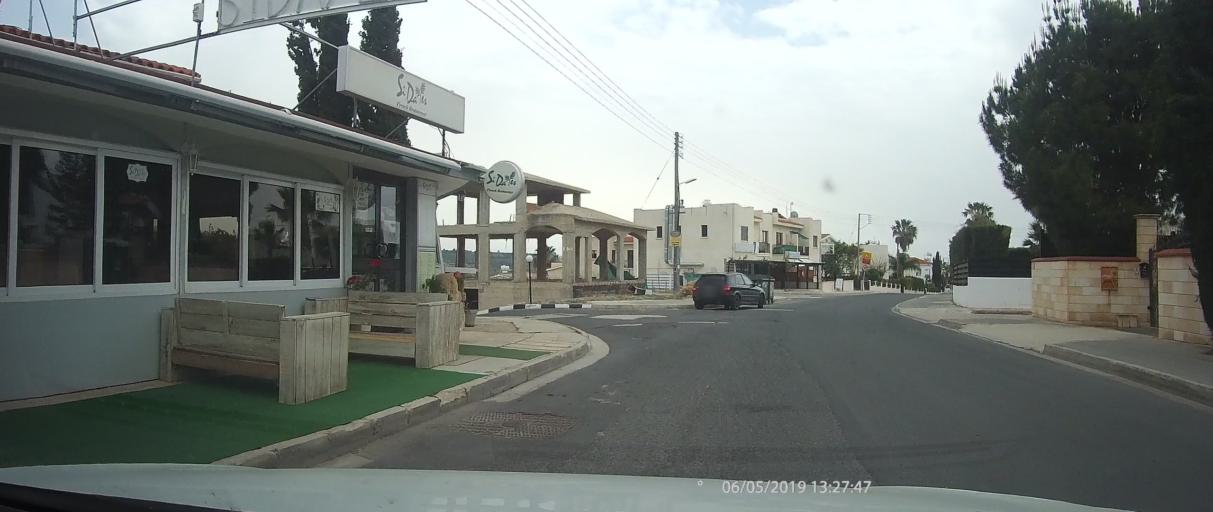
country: CY
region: Pafos
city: Pegeia
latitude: 34.8532
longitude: 32.3801
